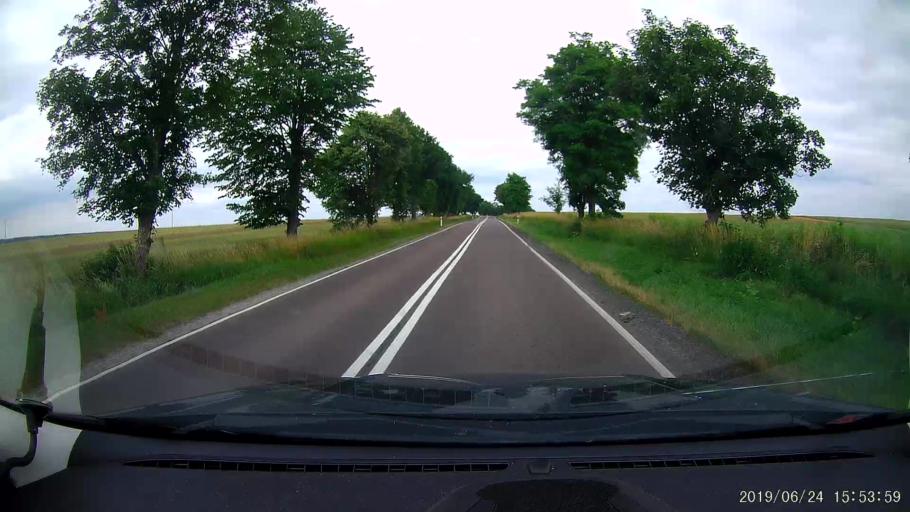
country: PL
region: Subcarpathian Voivodeship
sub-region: Powiat lubaczowski
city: Cieszanow
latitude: 50.2118
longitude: 23.1117
